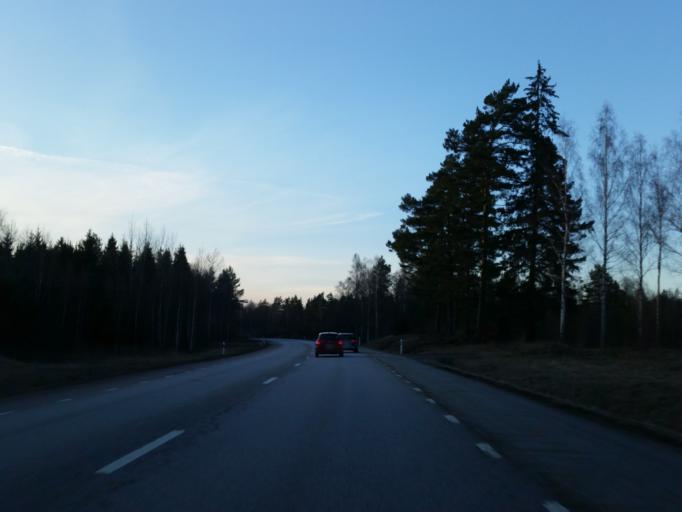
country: SE
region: Kalmar
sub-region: Oskarshamns Kommun
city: Oskarshamn
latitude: 57.4909
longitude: 16.5172
